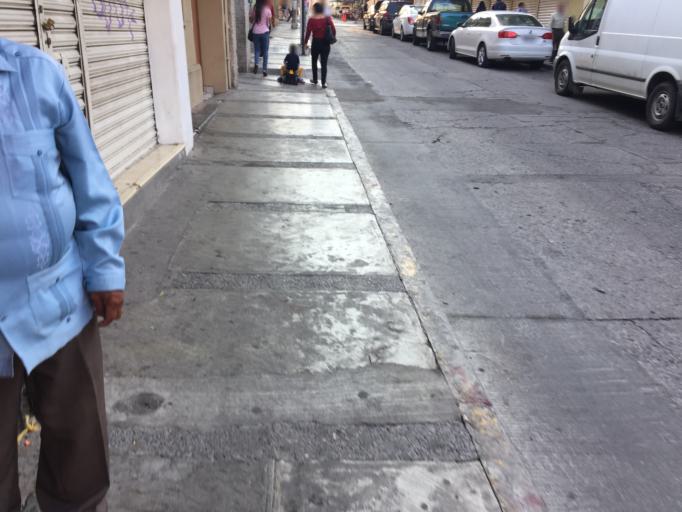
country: MX
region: Guerrero
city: Chilpancingo de los Bravos
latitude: 17.5527
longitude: -99.5007
